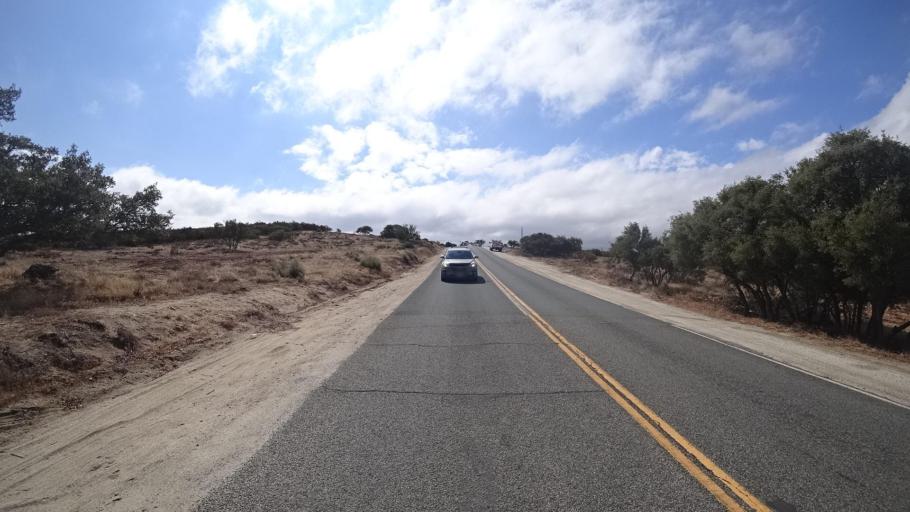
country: US
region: California
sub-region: San Diego County
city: Campo
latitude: 32.6653
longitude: -116.3167
